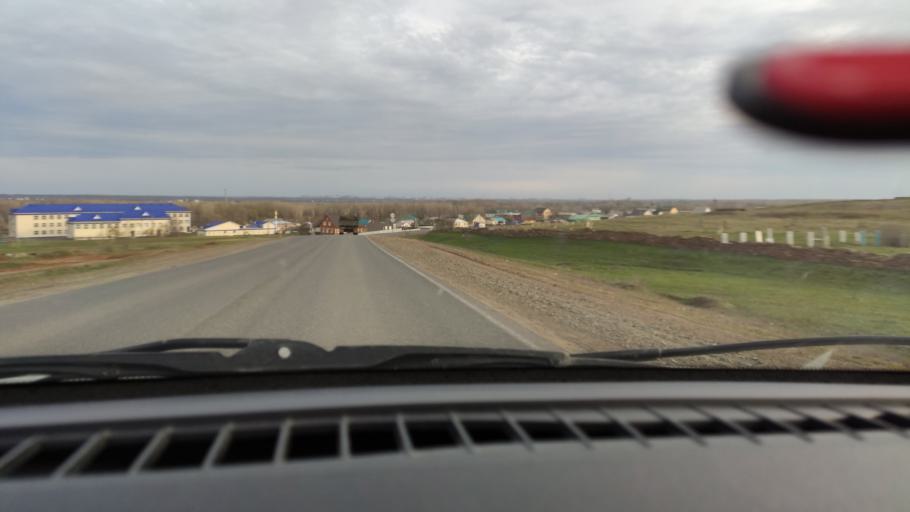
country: RU
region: Orenburg
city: Tatarskaya Kargala
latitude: 51.9511
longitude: 55.1823
